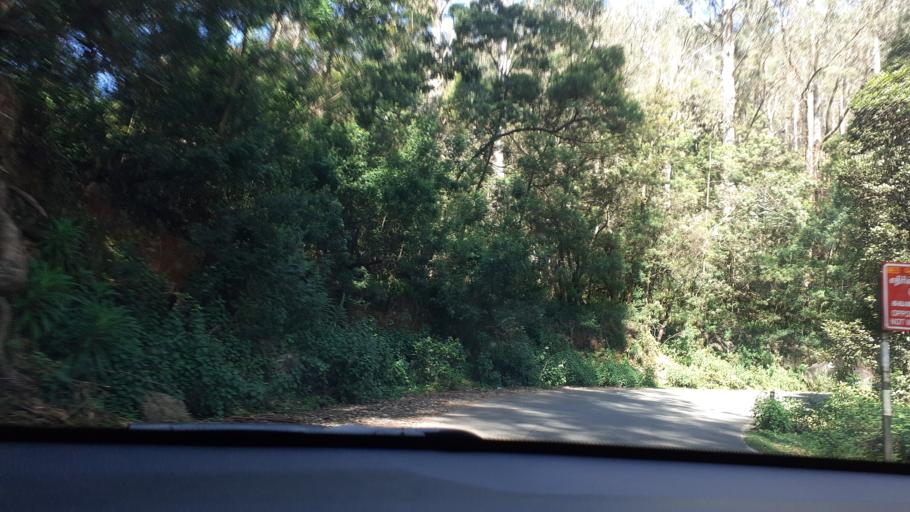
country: IN
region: Tamil Nadu
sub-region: Dindigul
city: Kodaikanal
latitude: 10.2232
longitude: 77.4208
